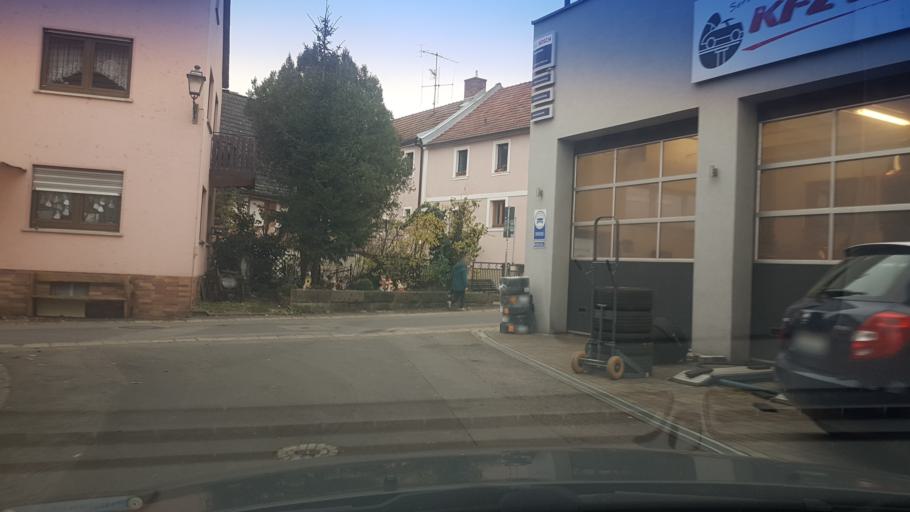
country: DE
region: Bavaria
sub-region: Upper Franconia
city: Baunach
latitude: 49.9852
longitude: 10.8519
